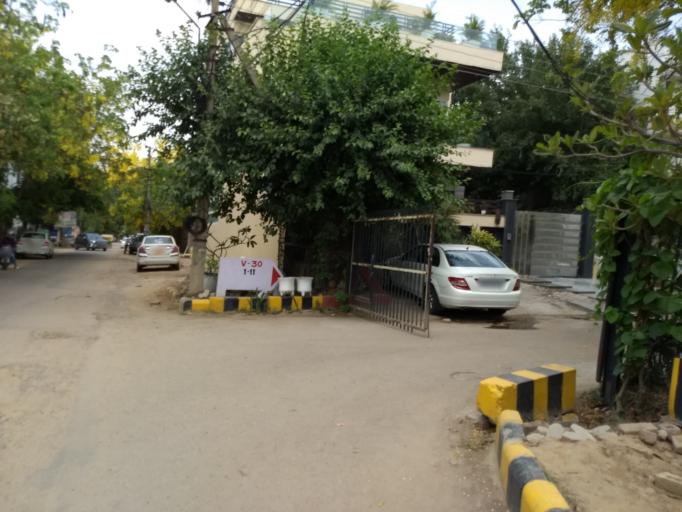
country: IN
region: Haryana
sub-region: Gurgaon
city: Gurgaon
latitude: 28.4954
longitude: 77.1038
